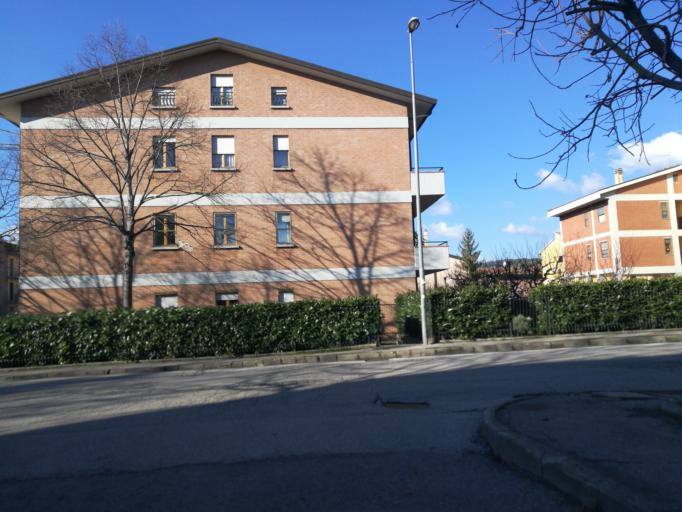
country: IT
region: Umbria
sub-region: Provincia di Perugia
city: Perugia
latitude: 43.0805
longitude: 12.3675
